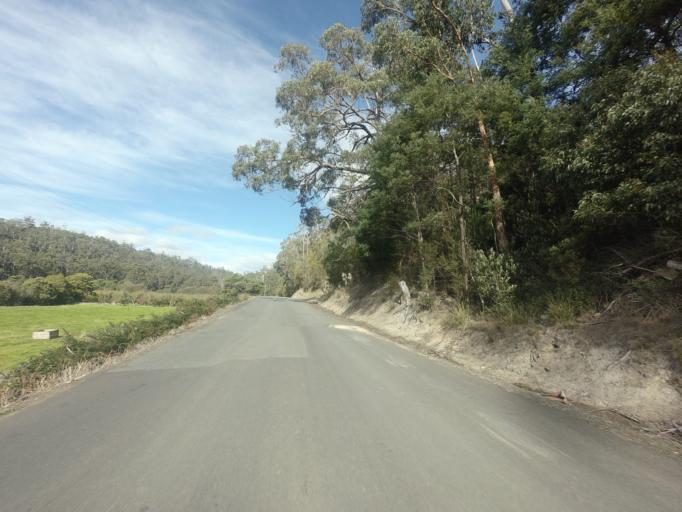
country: AU
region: Tasmania
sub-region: Clarence
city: Sandford
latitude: -43.1205
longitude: 147.7589
